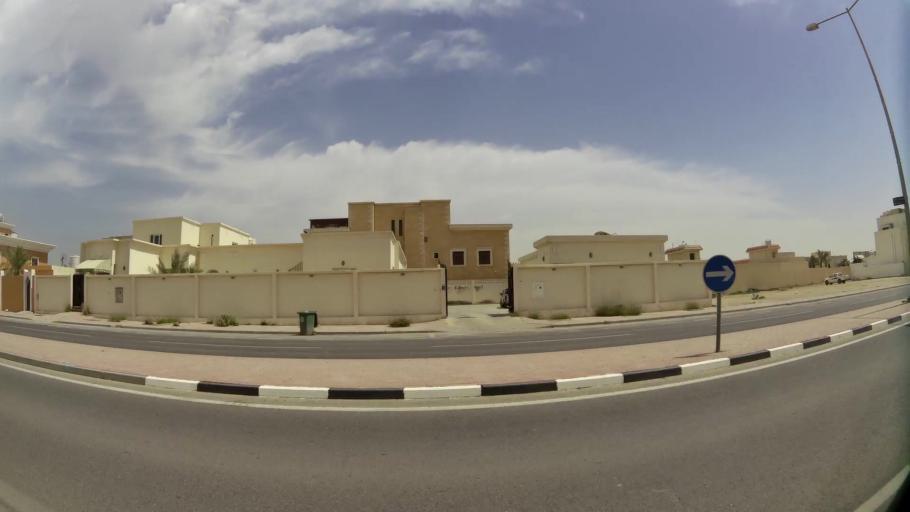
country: QA
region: Baladiyat ar Rayyan
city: Ar Rayyan
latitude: 25.2749
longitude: 51.4204
